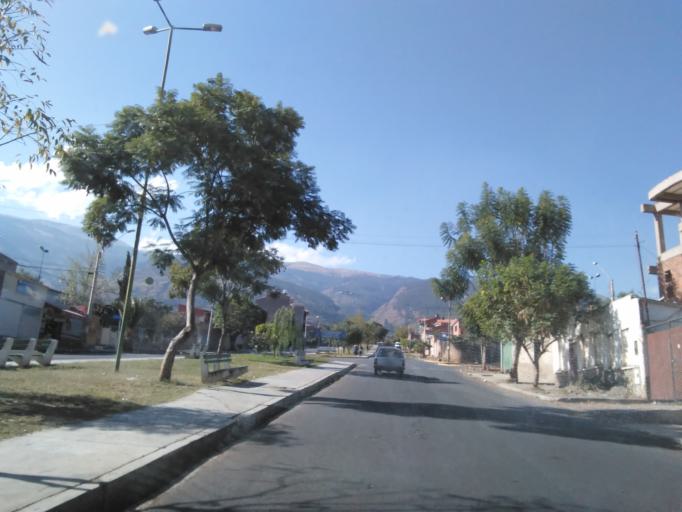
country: BO
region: Cochabamba
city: Cochabamba
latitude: -17.3533
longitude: -66.1640
